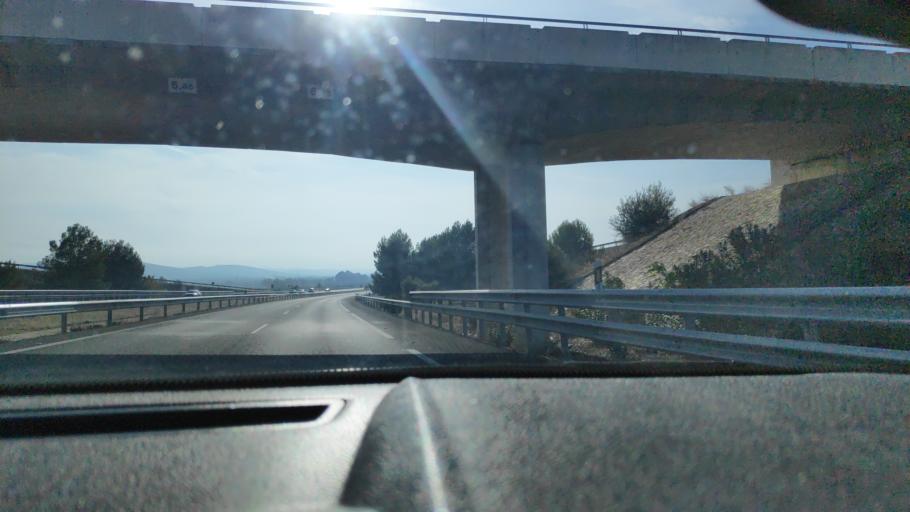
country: ES
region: Andalusia
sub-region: Provincia de Jaen
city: Mengibar
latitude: 37.9093
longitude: -3.7851
